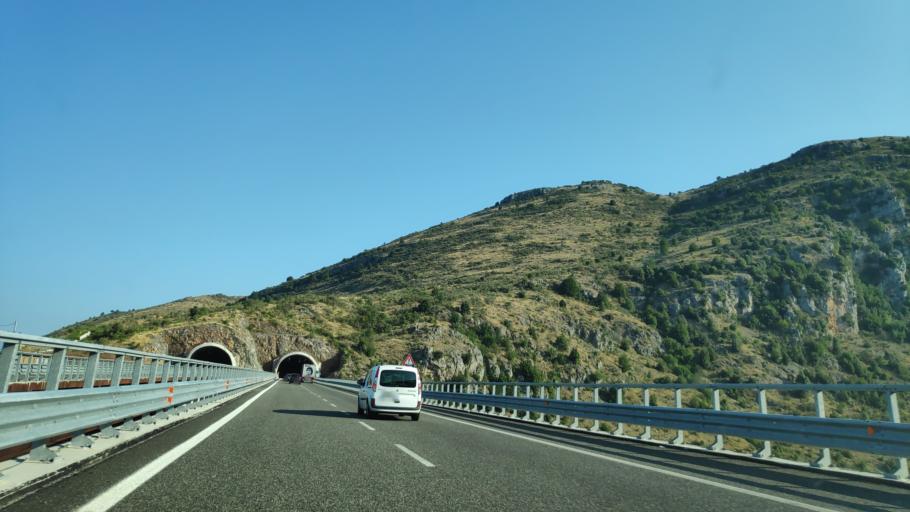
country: IT
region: Basilicate
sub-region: Provincia di Potenza
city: Lauria
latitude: 40.0358
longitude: 15.8738
